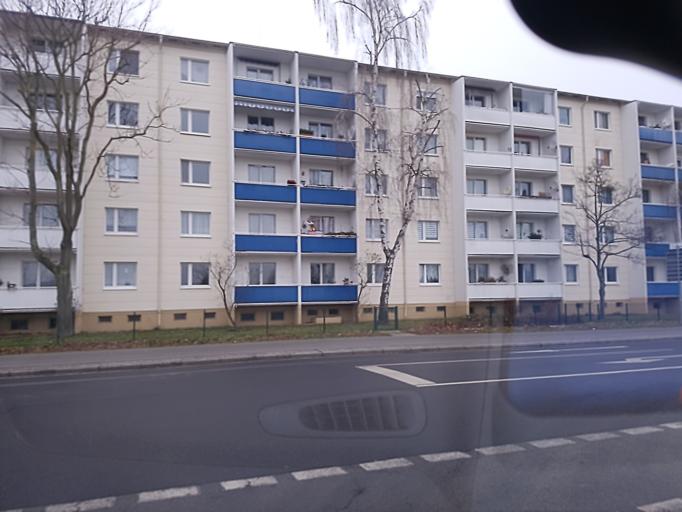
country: DE
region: Brandenburg
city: Lubbenau
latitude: 51.8640
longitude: 13.9416
